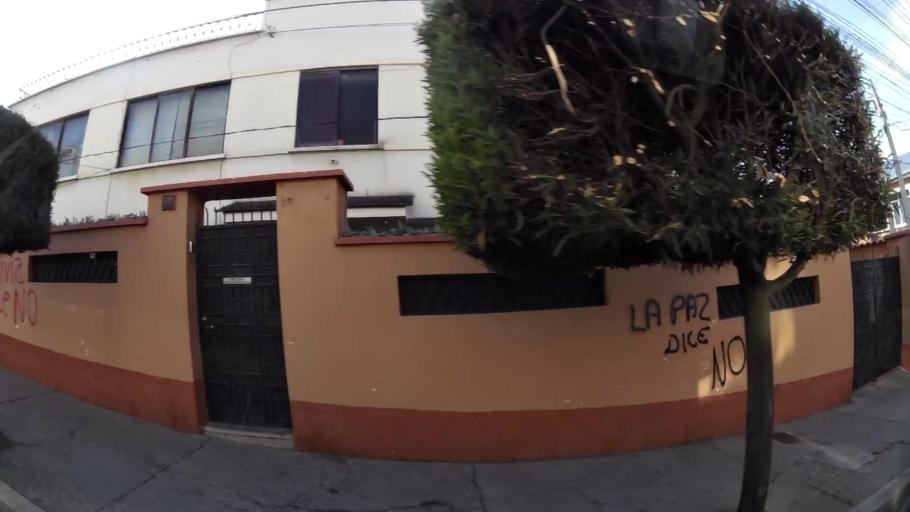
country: BO
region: La Paz
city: La Paz
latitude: -16.4935
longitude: -68.1231
